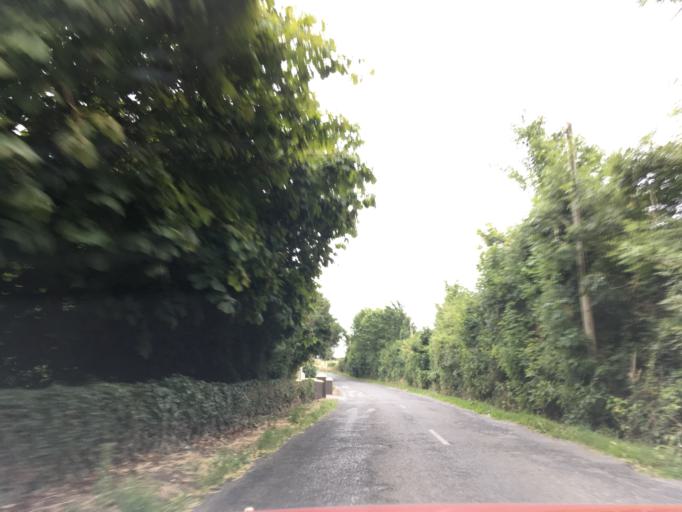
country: IE
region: Munster
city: Cashel
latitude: 52.4683
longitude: -7.8473
